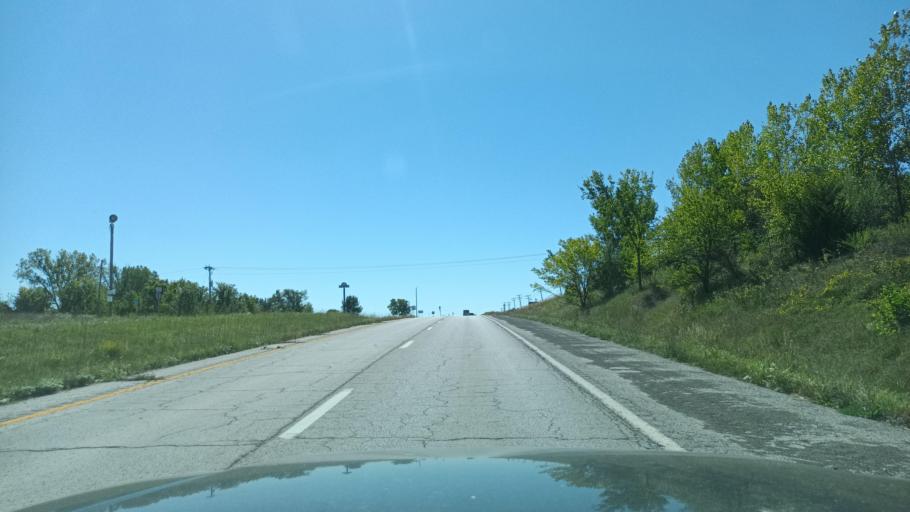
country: US
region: Missouri
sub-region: Adair County
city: Kirksville
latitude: 40.1619
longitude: -92.5722
